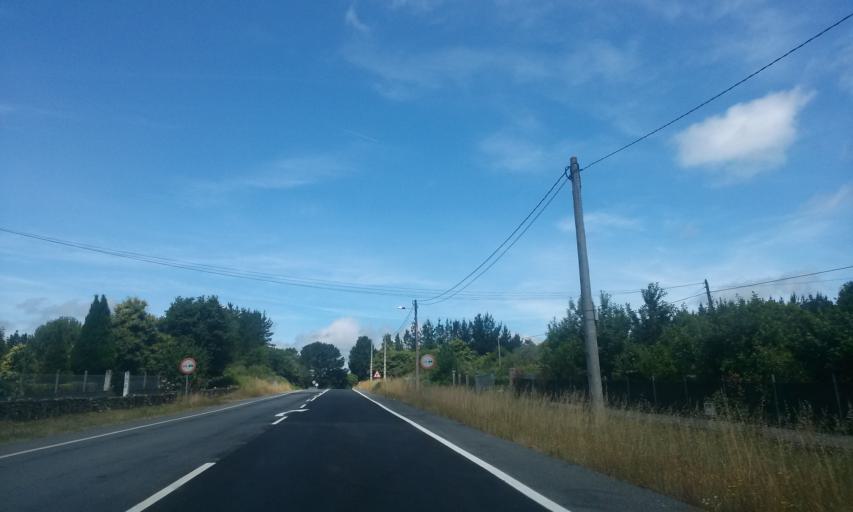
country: ES
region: Galicia
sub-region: Provincia de Lugo
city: Lugo
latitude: 43.0074
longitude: -7.6484
